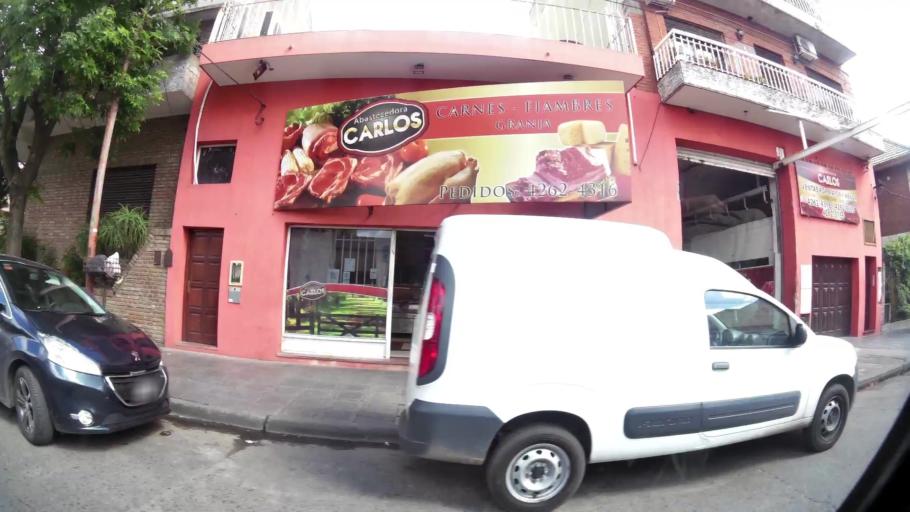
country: AR
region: Buenos Aires
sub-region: Partido de Lanus
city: Lanus
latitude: -34.6922
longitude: -58.4073
